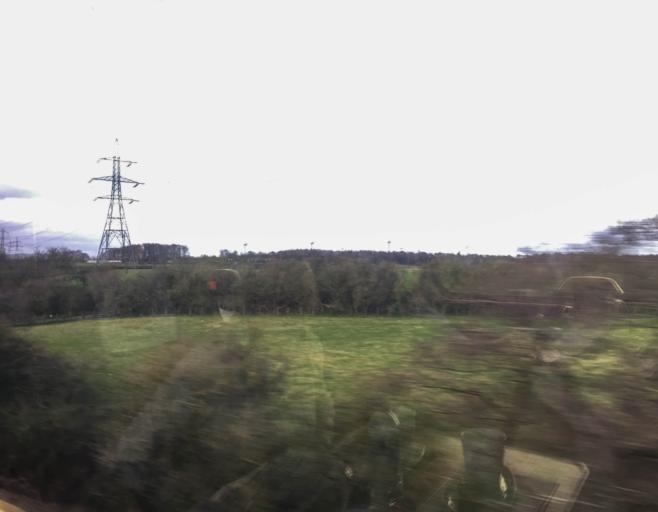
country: GB
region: Scotland
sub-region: Dumfries and Galloway
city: Gretna
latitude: 54.9928
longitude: -3.0389
